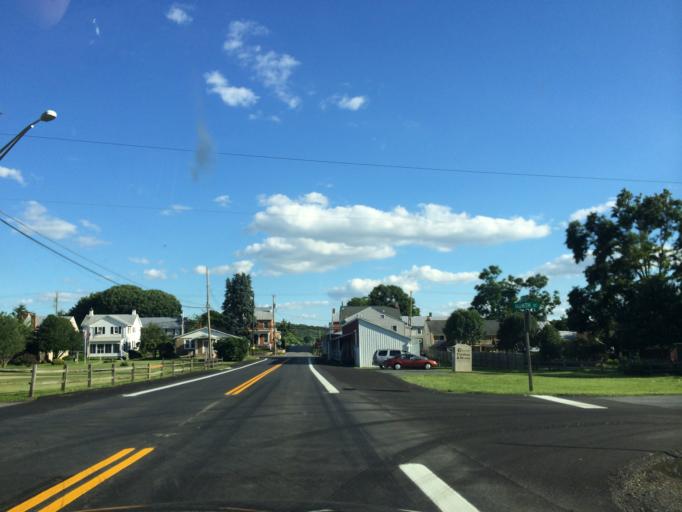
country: US
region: Maryland
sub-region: Frederick County
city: Linganore
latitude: 39.4858
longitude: -77.2469
